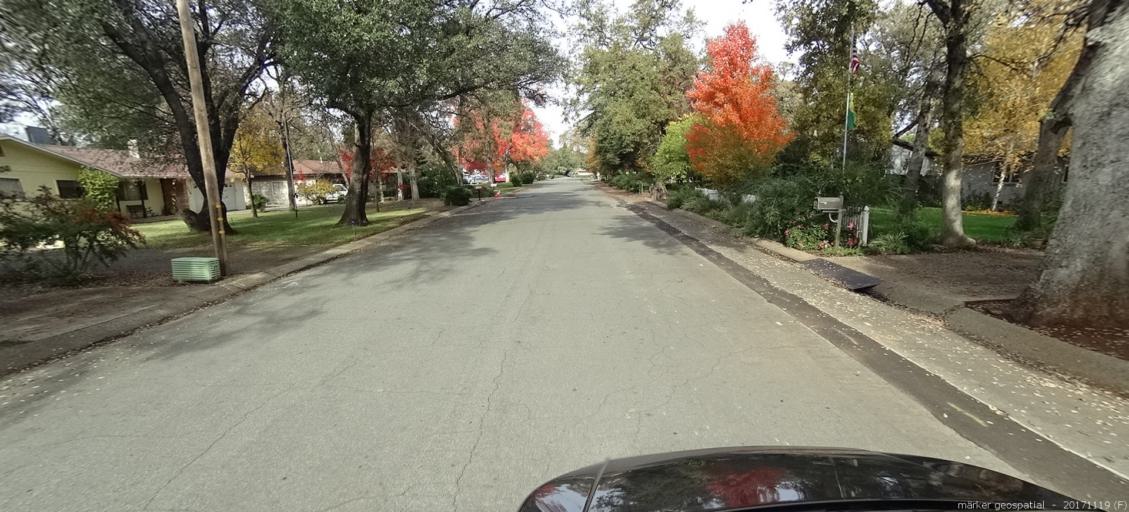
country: US
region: California
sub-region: Shasta County
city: Anderson
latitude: 40.4928
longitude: -122.3098
